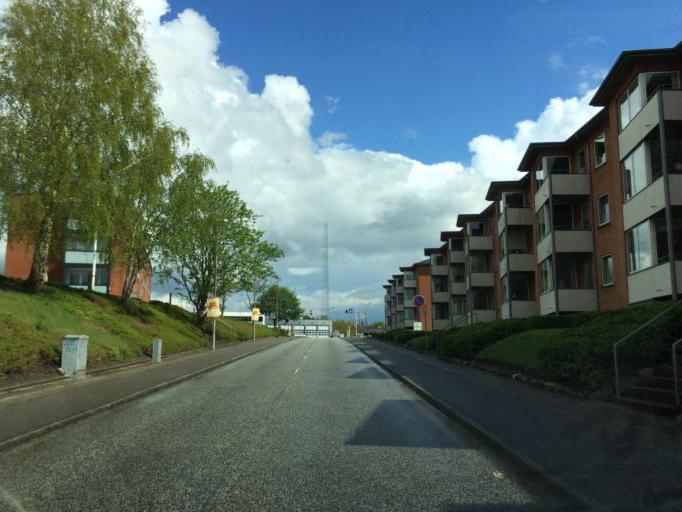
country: DK
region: Central Jutland
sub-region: Holstebro Kommune
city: Holstebro
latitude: 56.3588
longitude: 8.6096
